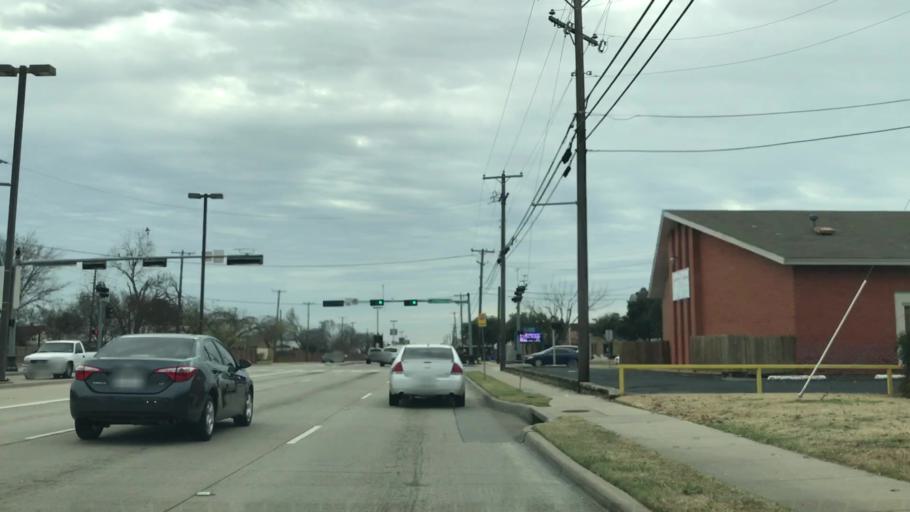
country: US
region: Texas
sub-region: Dallas County
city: Carrollton
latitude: 32.9497
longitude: -96.8904
